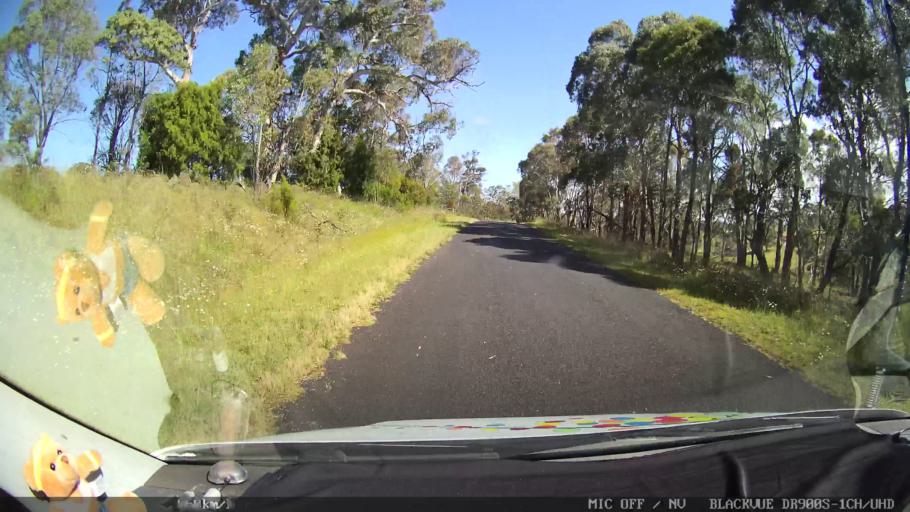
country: AU
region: New South Wales
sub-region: Guyra
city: Guyra
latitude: -30.0627
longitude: 151.6653
